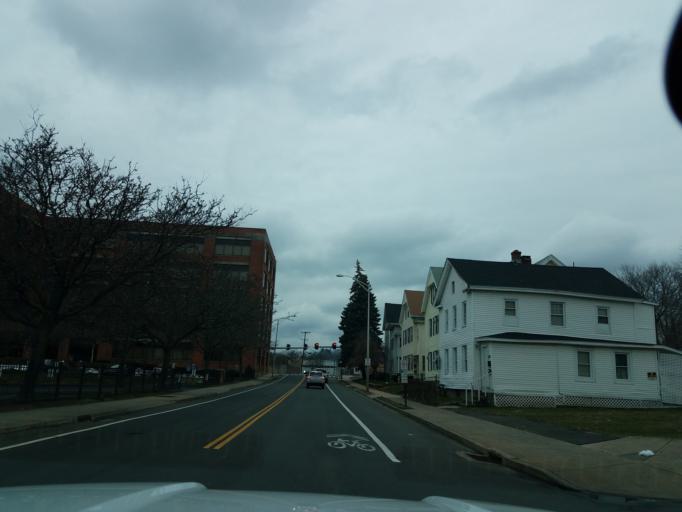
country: US
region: Connecticut
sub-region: Hartford County
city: New Britain
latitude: 41.6698
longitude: -72.7963
